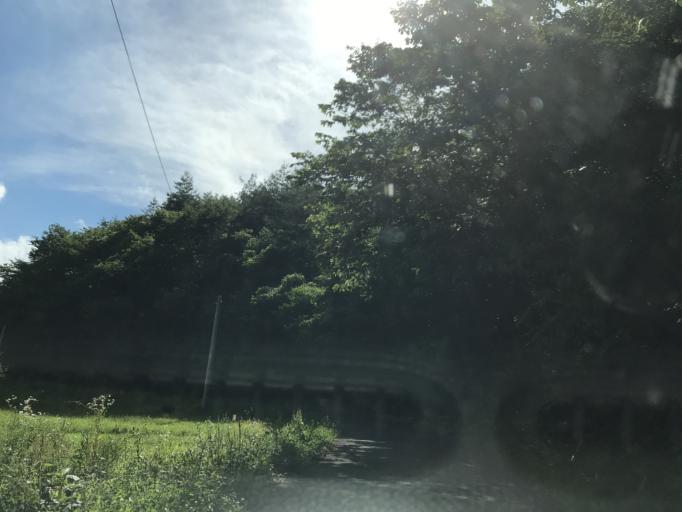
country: JP
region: Iwate
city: Ichinoseki
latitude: 38.9346
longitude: 141.0070
